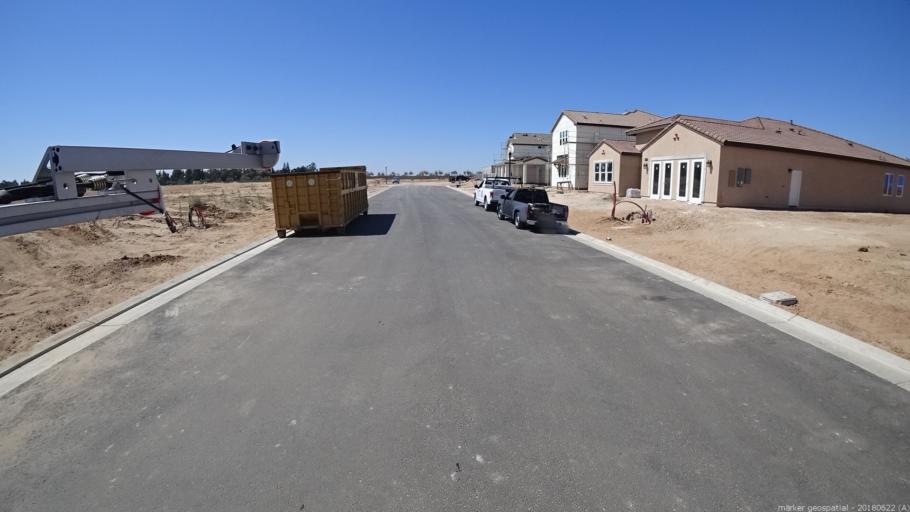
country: US
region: California
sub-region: Madera County
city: Bonadelle Ranchos-Madera Ranchos
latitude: 36.9163
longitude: -119.8046
